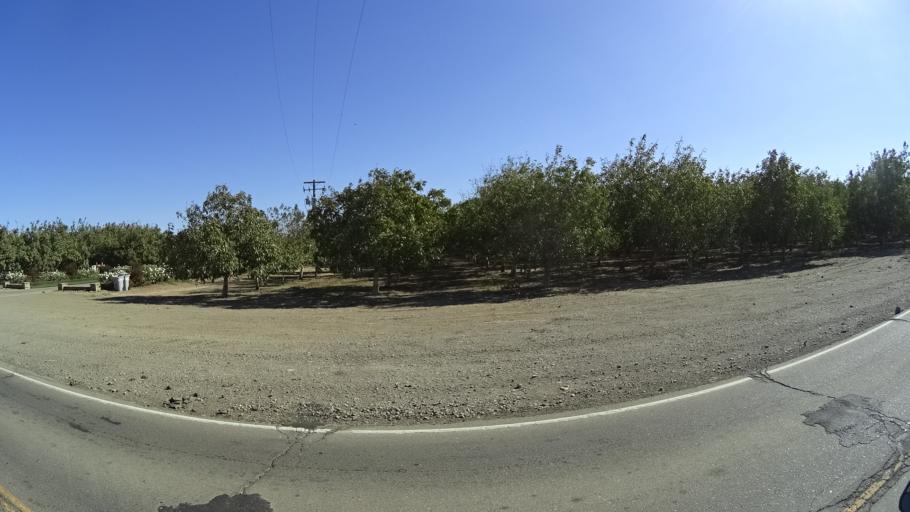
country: US
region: California
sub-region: Yolo County
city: Winters
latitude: 38.5681
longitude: -121.9713
